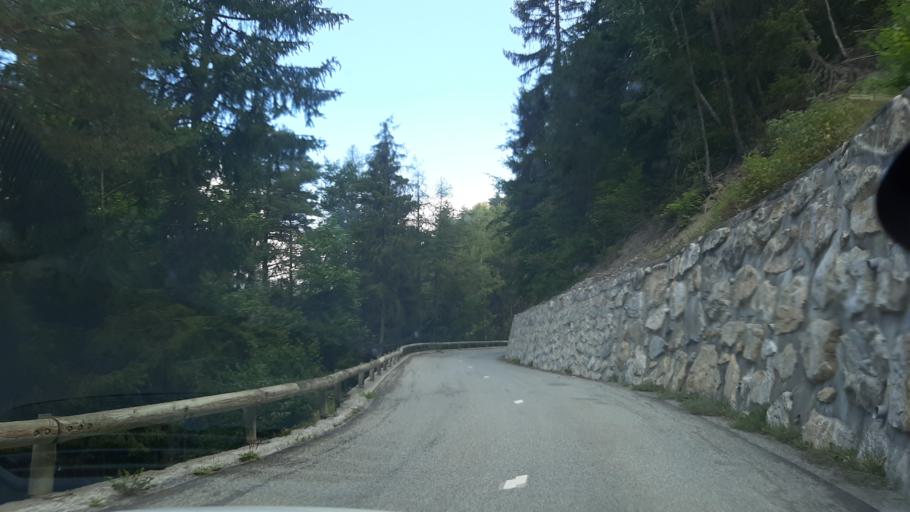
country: FR
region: Rhone-Alpes
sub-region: Departement de la Savoie
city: Aime
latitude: 45.5261
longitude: 6.6171
